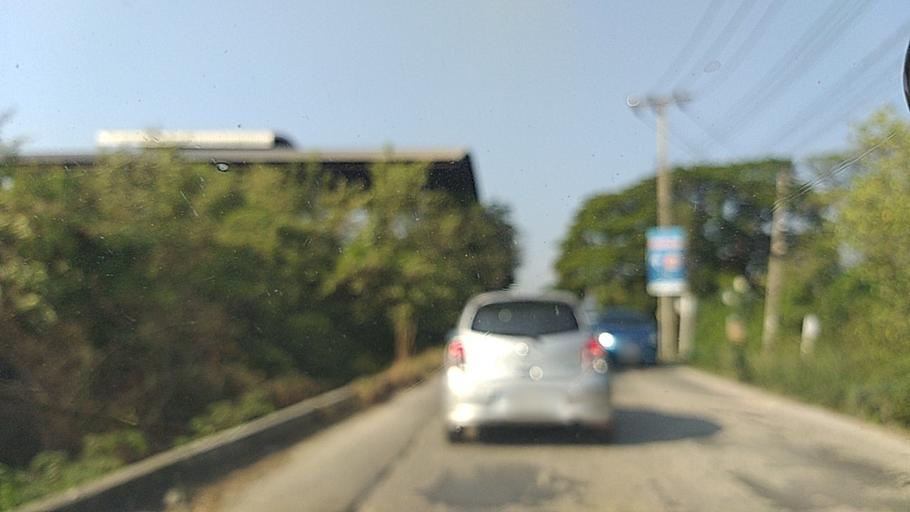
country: TH
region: Nonthaburi
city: Bang Bua Thong
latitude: 13.9349
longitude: 100.3805
